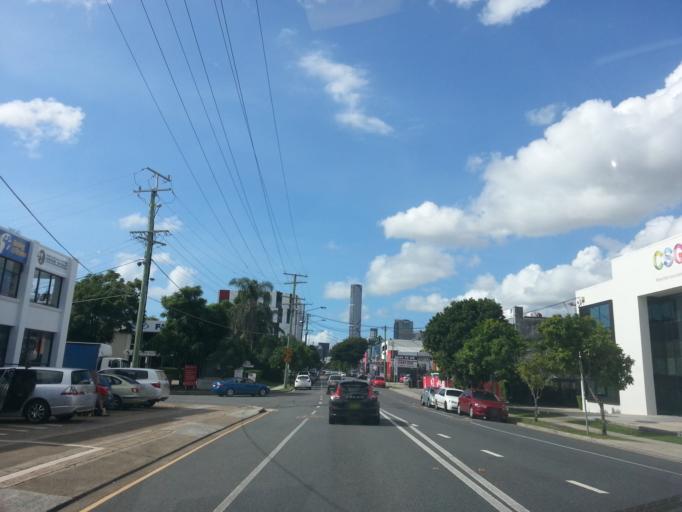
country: AU
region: Queensland
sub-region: Brisbane
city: Milton
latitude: -27.4780
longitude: 153.0068
